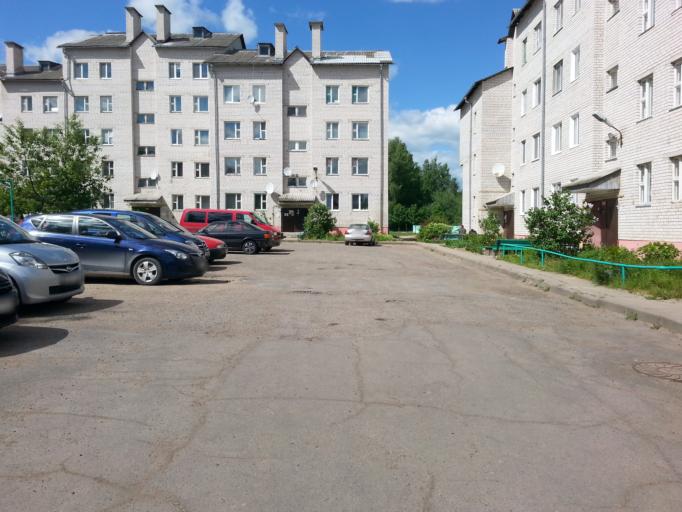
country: BY
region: Minsk
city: Narach
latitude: 54.9175
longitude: 26.6984
